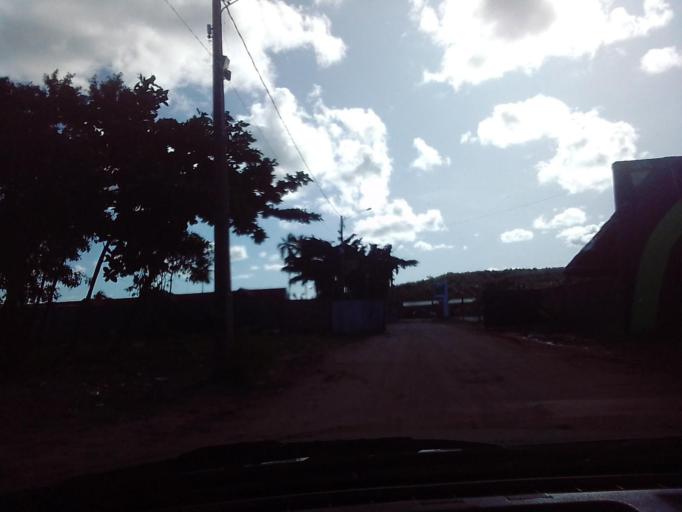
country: BR
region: Pernambuco
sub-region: Igarassu
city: Igarassu
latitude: -7.8614
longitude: -34.8383
